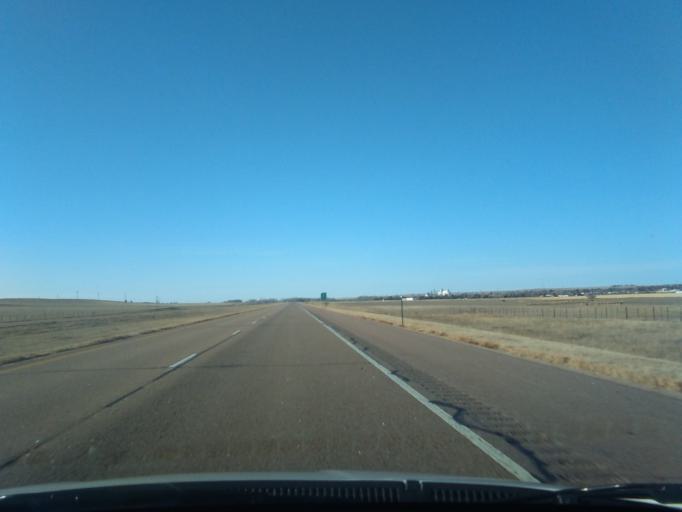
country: US
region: Nebraska
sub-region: Deuel County
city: Chappell
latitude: 41.0667
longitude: -102.4495
